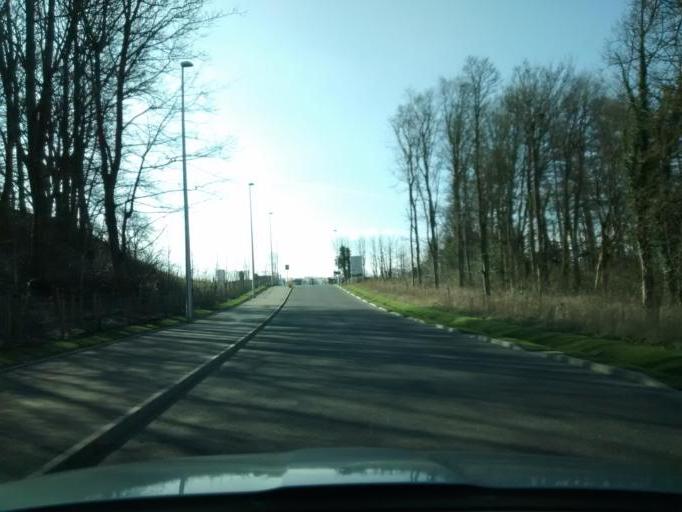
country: GB
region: Scotland
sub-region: West Lothian
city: East Calder
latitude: 55.8989
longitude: -3.4544
